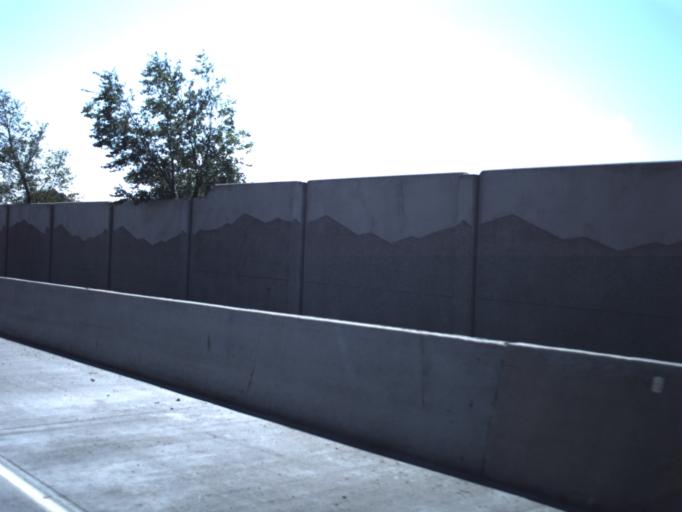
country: US
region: Utah
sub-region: Salt Lake County
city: Salt Lake City
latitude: 40.7600
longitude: -111.9152
